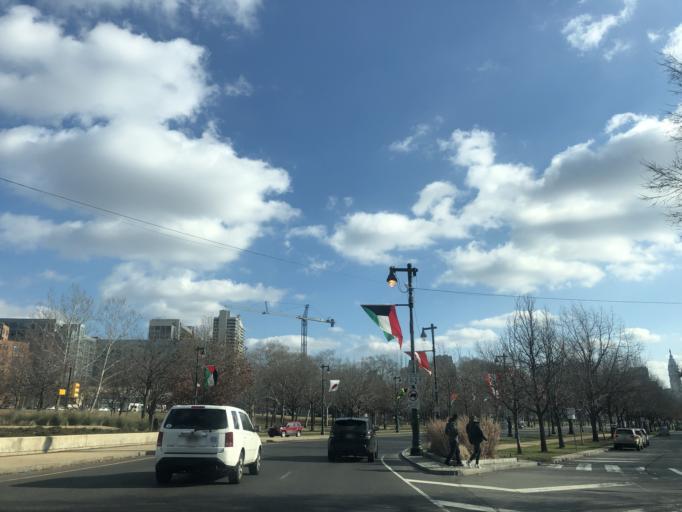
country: US
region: Pennsylvania
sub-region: Philadelphia County
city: Philadelphia
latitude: 39.9627
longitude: -75.1776
